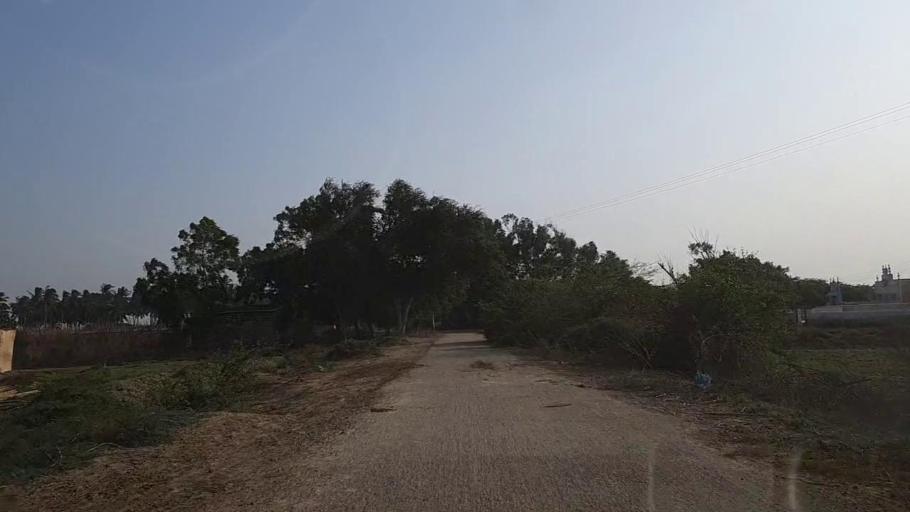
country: PK
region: Sindh
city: Keti Bandar
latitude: 24.1660
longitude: 67.6275
